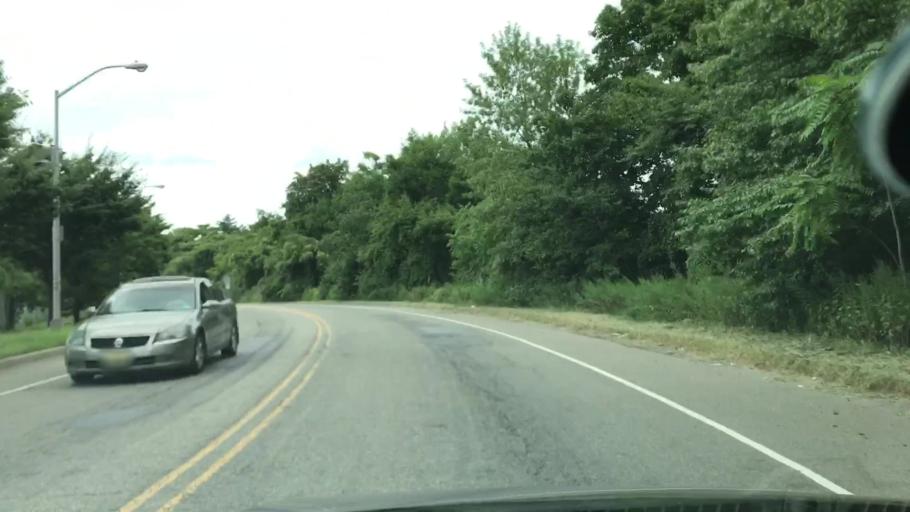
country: US
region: New Jersey
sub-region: Hudson County
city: Jersey City
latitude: 40.6958
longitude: -74.0790
